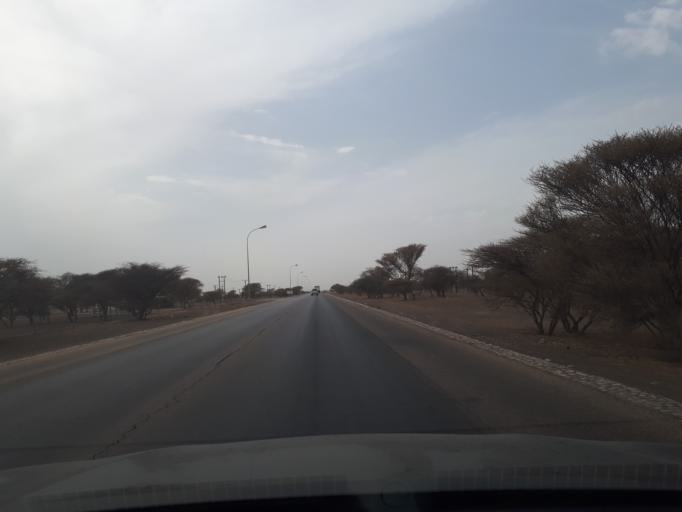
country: OM
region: Ash Sharqiyah
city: Badiyah
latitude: 22.4738
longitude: 58.7860
